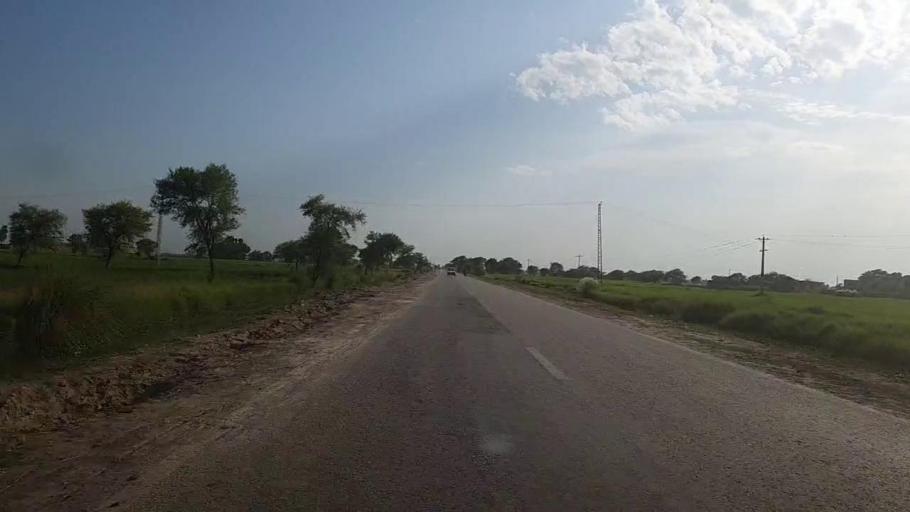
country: PK
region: Sindh
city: Thul
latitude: 28.2123
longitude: 68.7510
